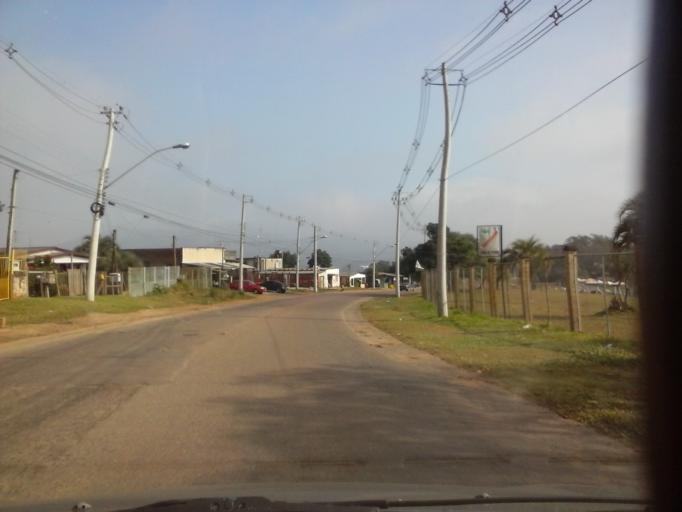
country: BR
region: Rio Grande do Sul
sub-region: Viamao
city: Viamao
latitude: -30.0491
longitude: -51.0754
